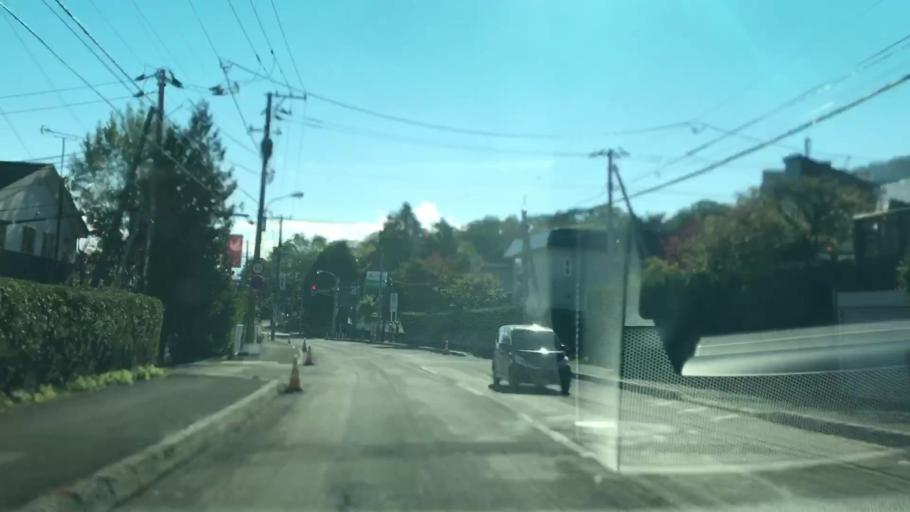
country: JP
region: Hokkaido
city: Sapporo
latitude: 43.0384
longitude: 141.3225
